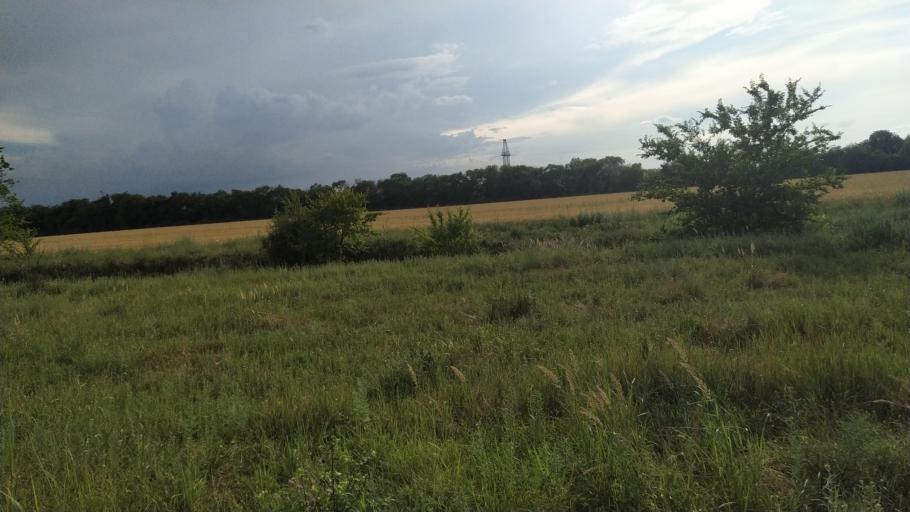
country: RU
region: Rostov
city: Bataysk
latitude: 47.1155
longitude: 39.7114
